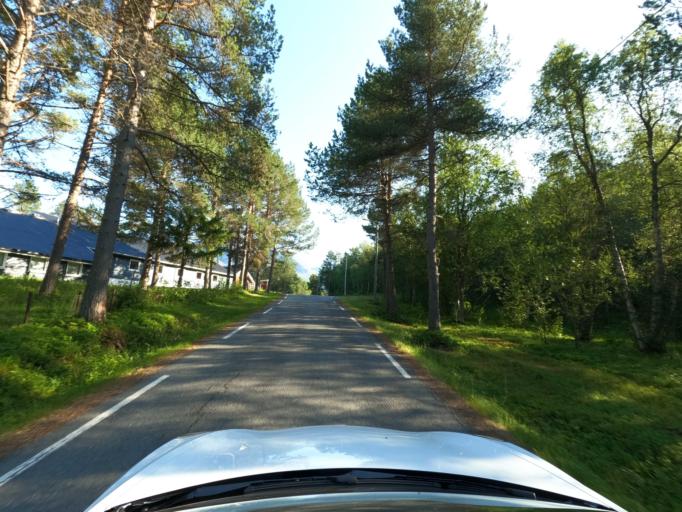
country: NO
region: Nordland
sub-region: Narvik
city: Bjerkvik
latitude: 68.4792
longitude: 17.5278
